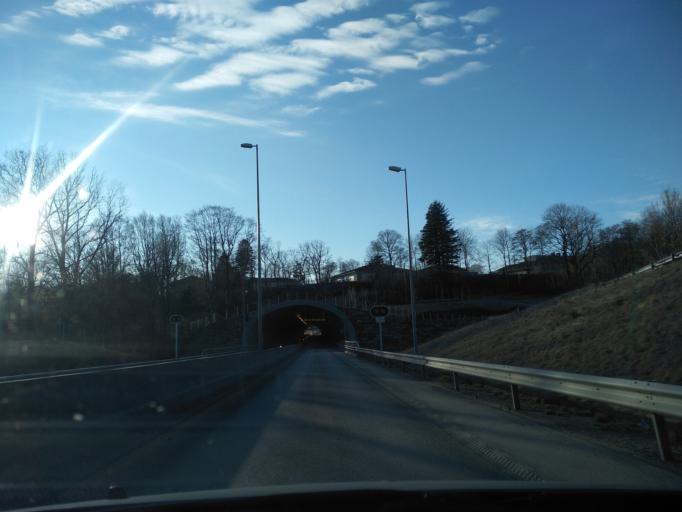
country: NO
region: Rogaland
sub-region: Tysvaer
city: Aksdal
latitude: 59.5058
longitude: 5.6005
